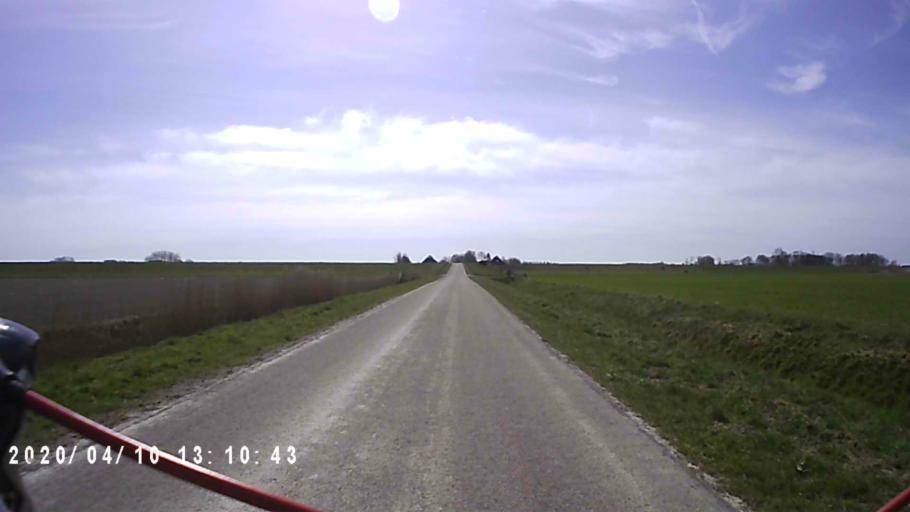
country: NL
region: Groningen
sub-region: Gemeente De Marne
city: Ulrum
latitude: 53.4087
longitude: 6.4190
